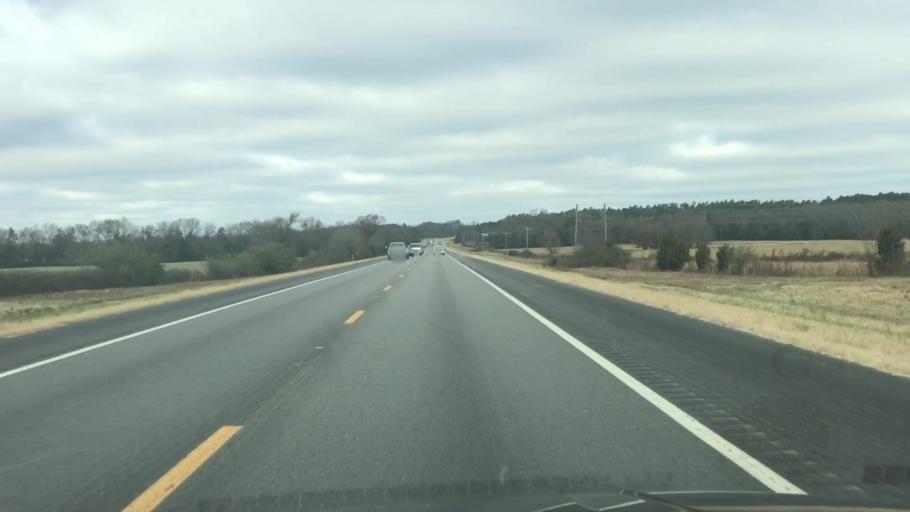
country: US
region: Arkansas
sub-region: Scott County
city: Waldron
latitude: 34.8774
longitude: -94.0955
